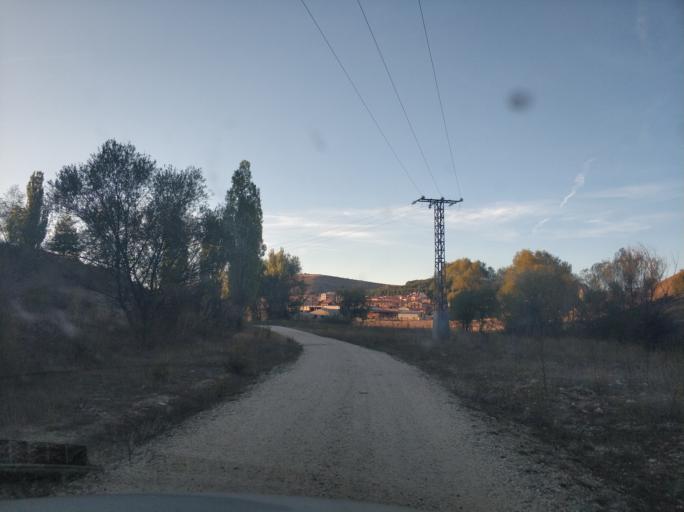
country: ES
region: Castille and Leon
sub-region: Provincia de Burgos
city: Hontoria del Pinar
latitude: 41.8431
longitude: -3.1613
